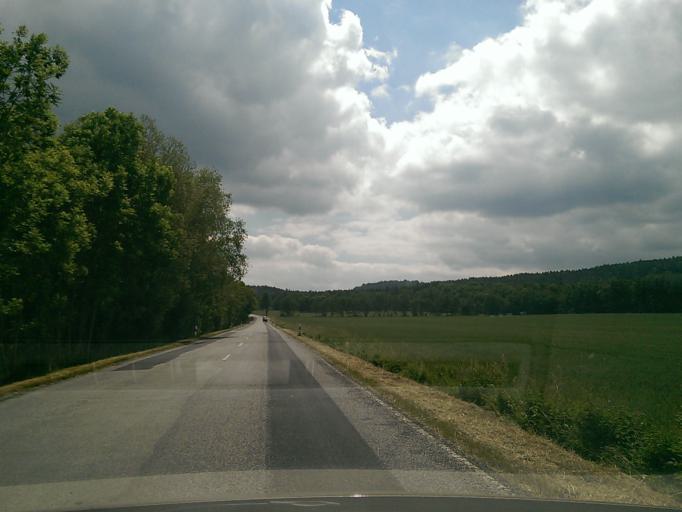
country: DE
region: Saxony
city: Kurort Jonsdorf
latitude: 50.8692
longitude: 14.6874
